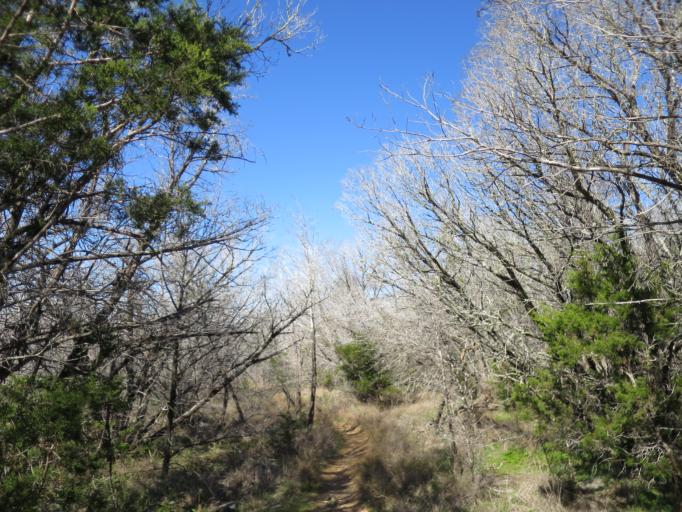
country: US
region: Texas
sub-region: Llano County
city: Kingsland
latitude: 30.6855
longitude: -98.3539
